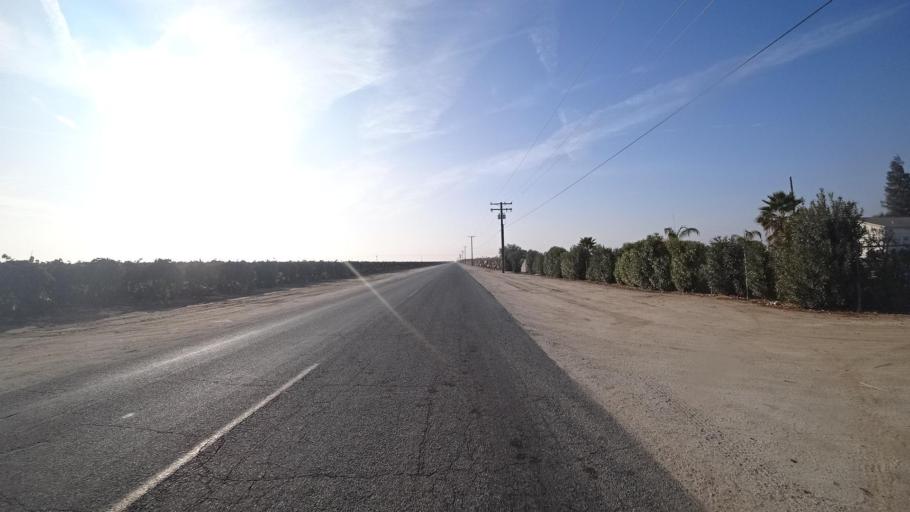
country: US
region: California
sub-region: Kern County
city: McFarland
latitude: 35.6783
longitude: -119.2048
